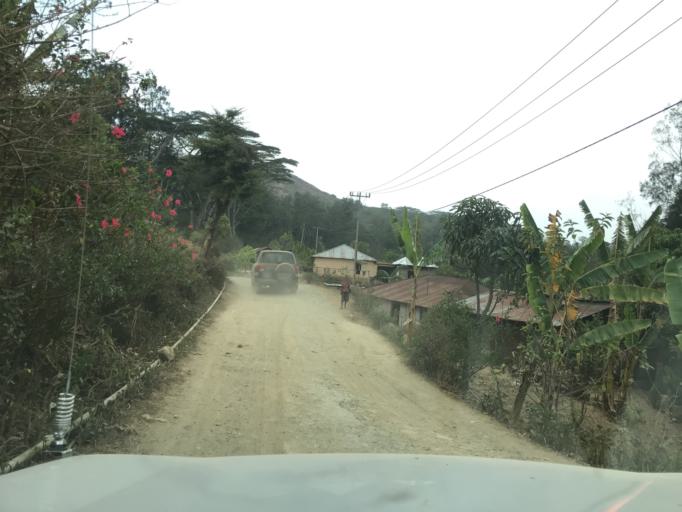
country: TL
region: Ermera
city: Gleno
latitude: -8.8327
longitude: 125.4516
